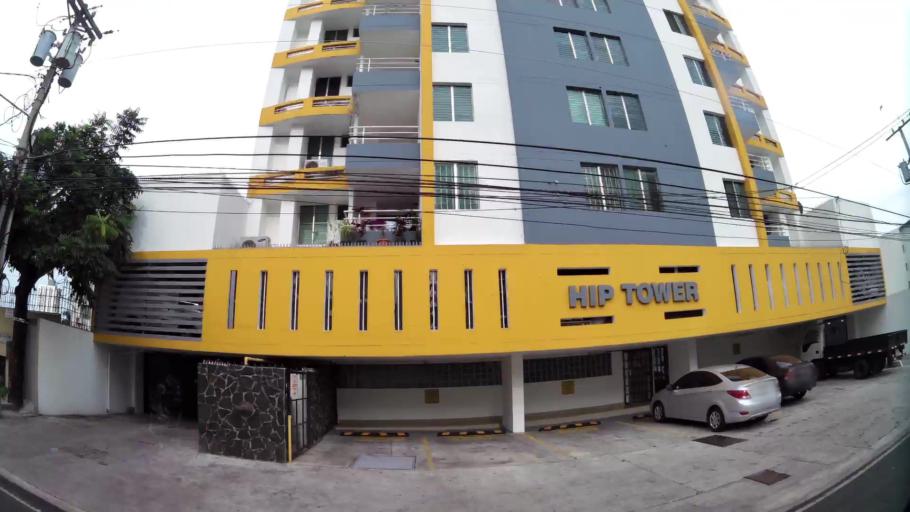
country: PA
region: Panama
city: Panama
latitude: 9.0063
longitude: -79.5053
